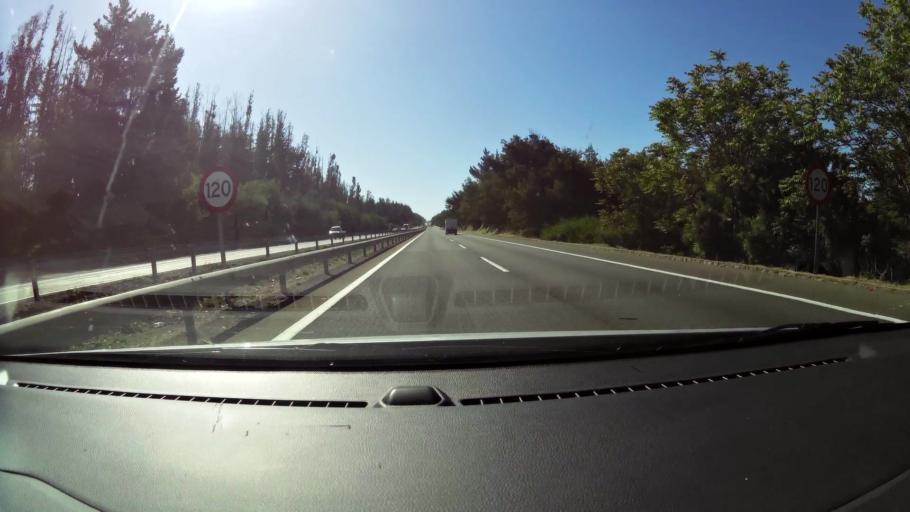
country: CL
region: Valparaiso
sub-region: Provincia de Marga Marga
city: Quilpue
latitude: -33.1729
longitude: -71.5191
